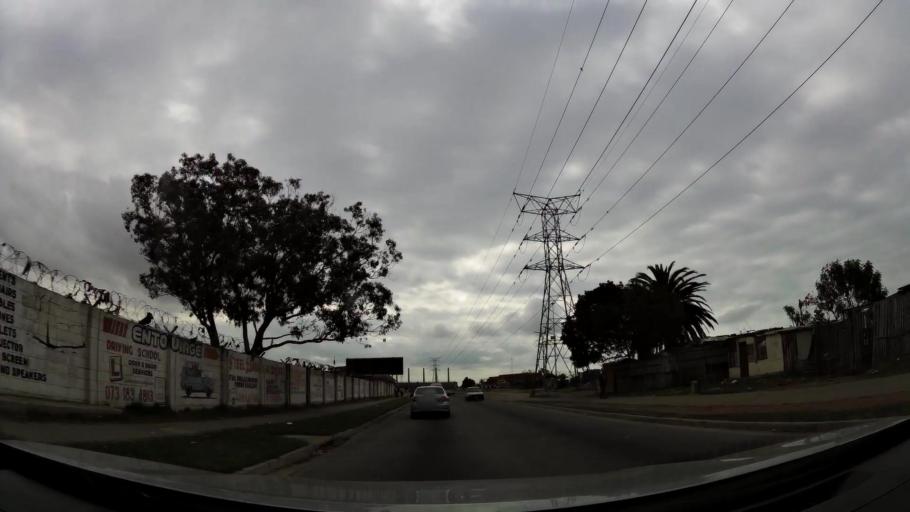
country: ZA
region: Eastern Cape
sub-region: Nelson Mandela Bay Metropolitan Municipality
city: Port Elizabeth
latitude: -33.8833
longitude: 25.5965
